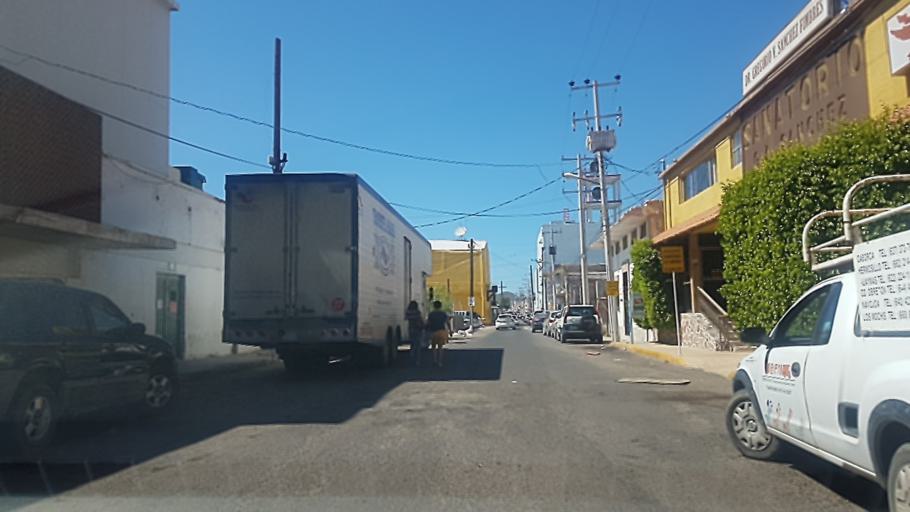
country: MX
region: Sonora
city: Heroica Guaymas
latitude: 27.9242
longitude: -110.8917
